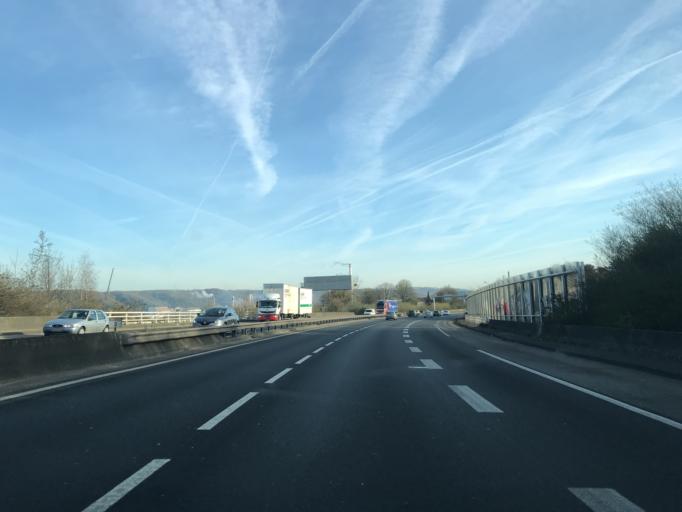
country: FR
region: Haute-Normandie
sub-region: Departement de la Seine-Maritime
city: Le Grand-Quevilly
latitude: 49.3984
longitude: 1.0320
